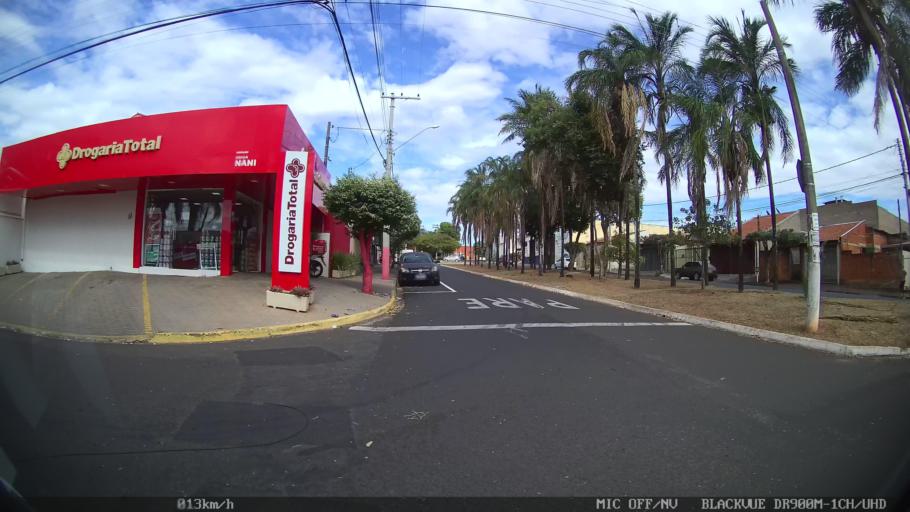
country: BR
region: Sao Paulo
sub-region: Sao Jose Do Rio Preto
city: Sao Jose do Rio Preto
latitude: -20.8066
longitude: -49.5040
